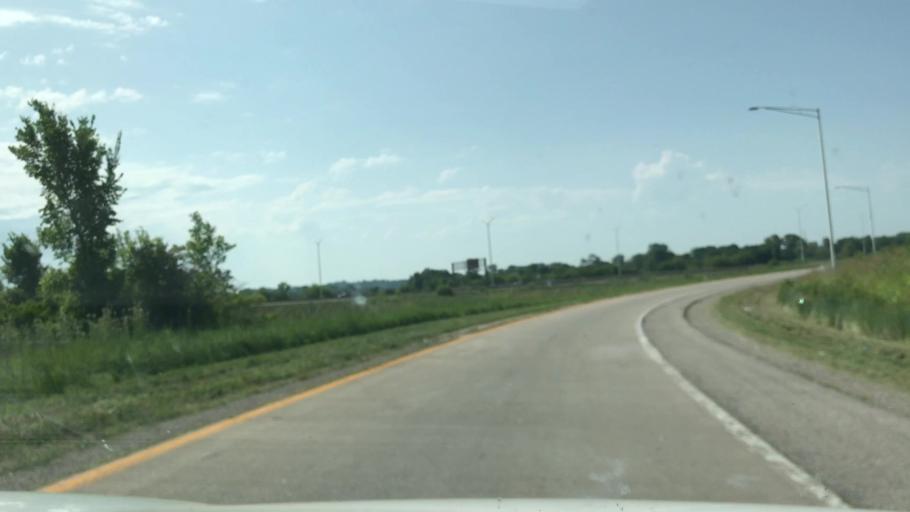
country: US
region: Illinois
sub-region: Saint Clair County
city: Washington Park
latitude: 38.6174
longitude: -90.0722
